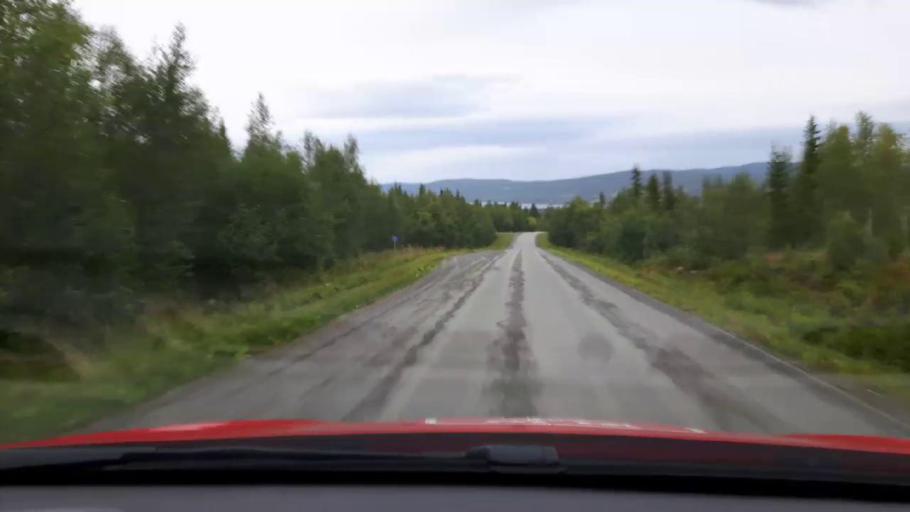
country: SE
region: Jaemtland
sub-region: Are Kommun
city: Are
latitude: 63.4334
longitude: 13.2122
